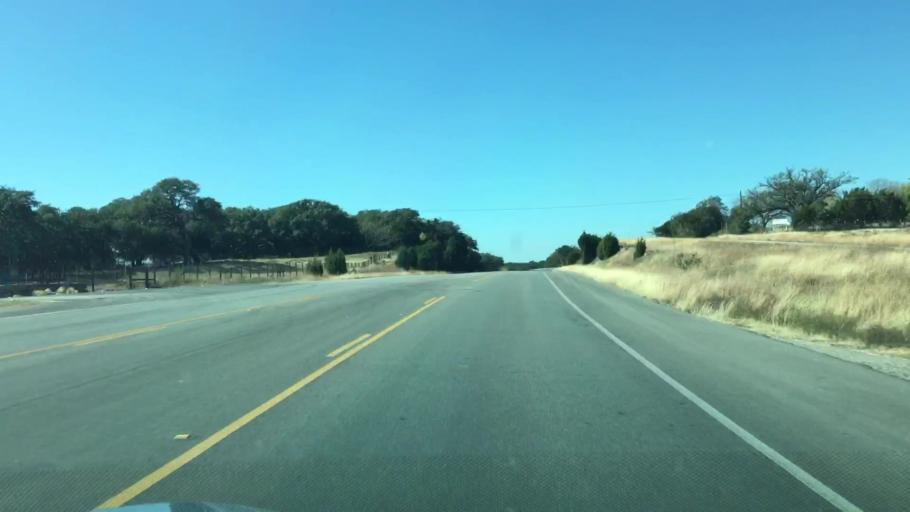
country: US
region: Texas
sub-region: Hays County
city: Dripping Springs
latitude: 30.2076
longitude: -98.1474
